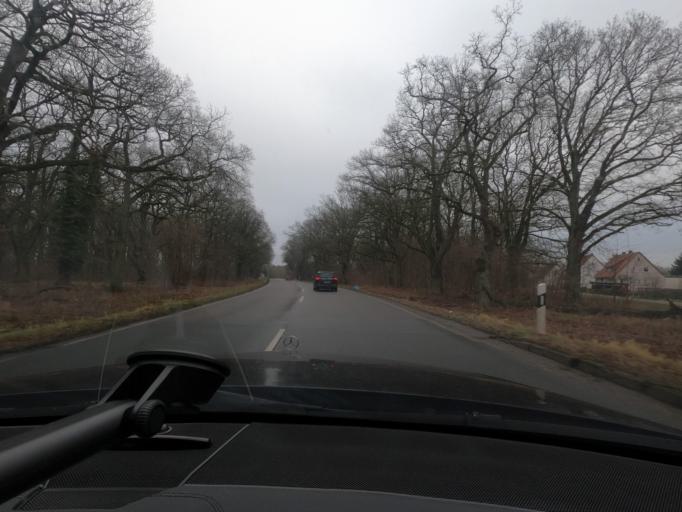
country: DE
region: Hesse
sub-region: Regierungsbezirk Kassel
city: Bad Arolsen
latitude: 51.3766
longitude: 9.0265
